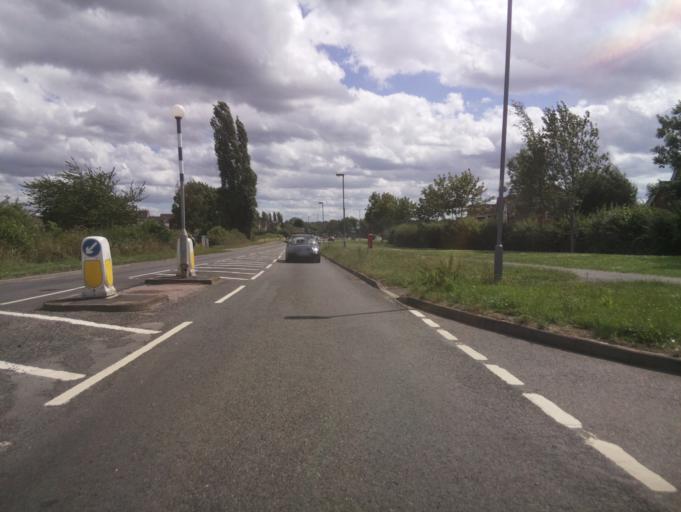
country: GB
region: England
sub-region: Nottinghamshire
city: East Leake
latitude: 52.8379
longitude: -1.1787
